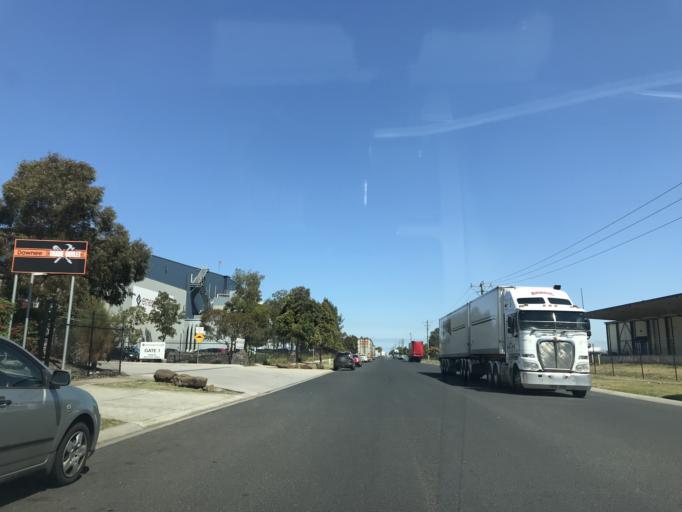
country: AU
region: Victoria
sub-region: Wyndham
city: Truganina
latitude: -37.8174
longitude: 144.7726
